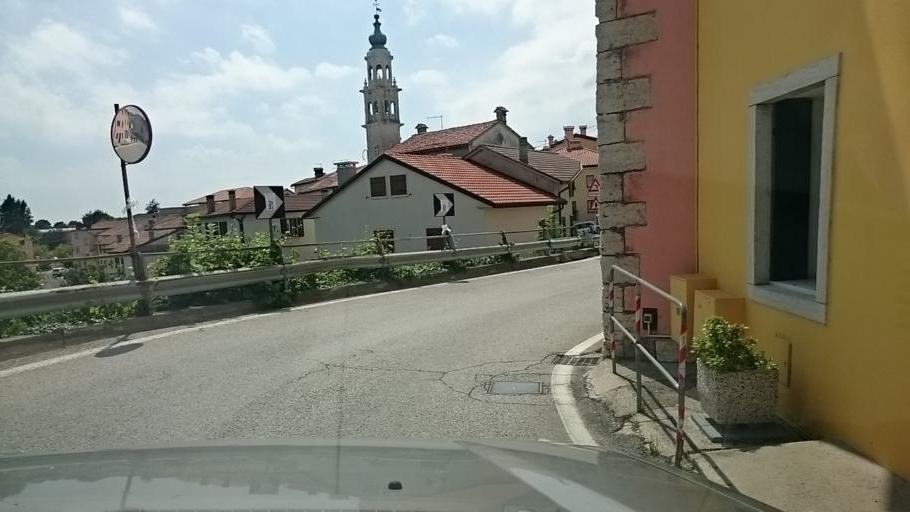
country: IT
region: Veneto
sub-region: Provincia di Vicenza
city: Conco
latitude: 45.7999
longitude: 11.6075
